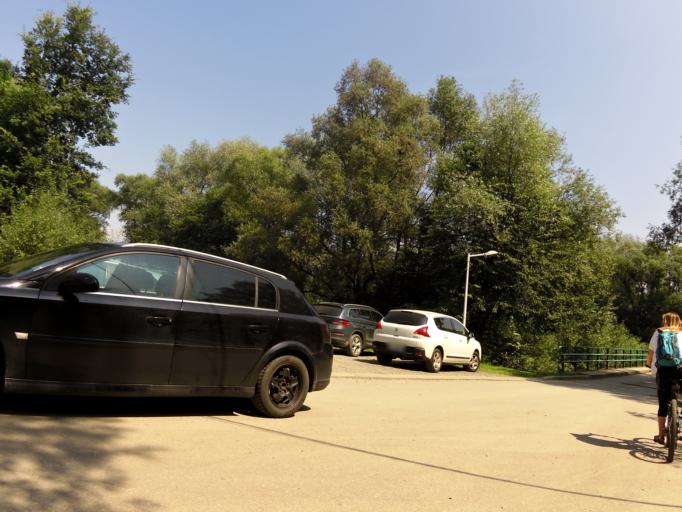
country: PL
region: Silesian Voivodeship
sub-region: Powiat zywiecki
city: Cisiec
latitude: 49.6025
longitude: 19.1051
